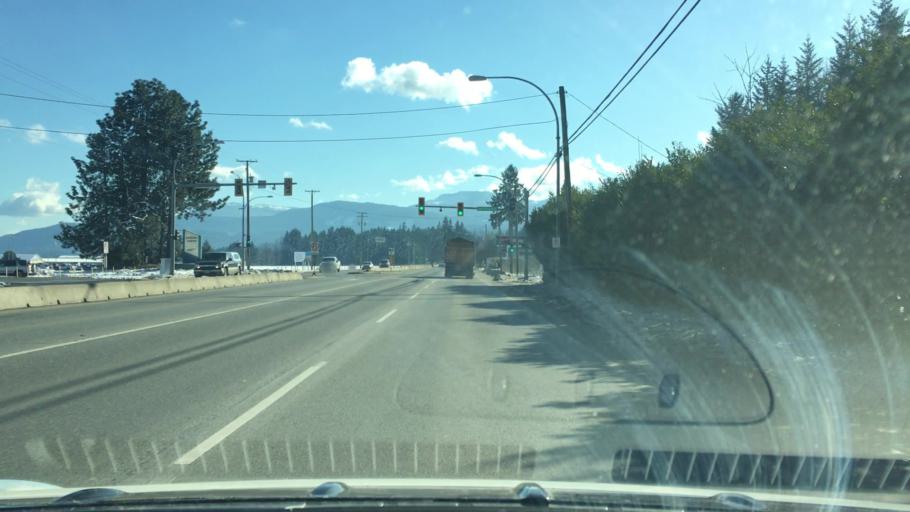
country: CA
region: British Columbia
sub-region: Cowichan Valley Regional District
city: Ladysmith
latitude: 49.0544
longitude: -123.8776
